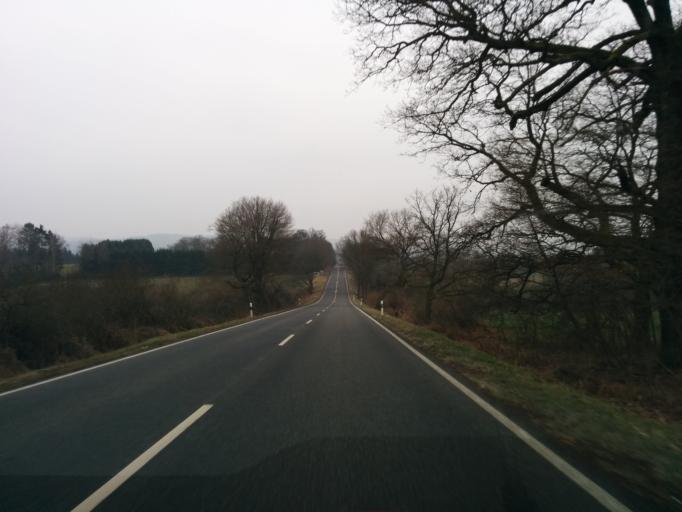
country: DE
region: Rheinland-Pfalz
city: Eitelborn
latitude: 50.3542
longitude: 7.7044
